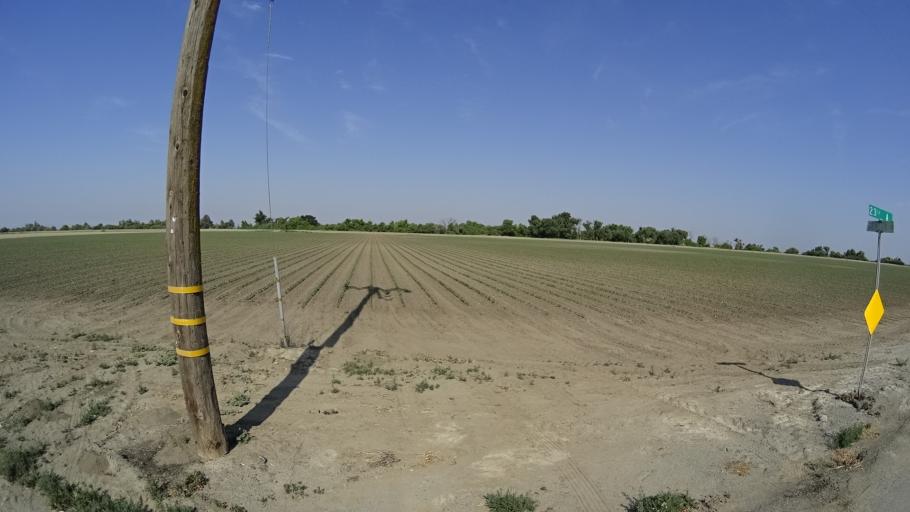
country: US
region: California
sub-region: Kings County
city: Lemoore Station
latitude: 36.3365
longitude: -119.8693
